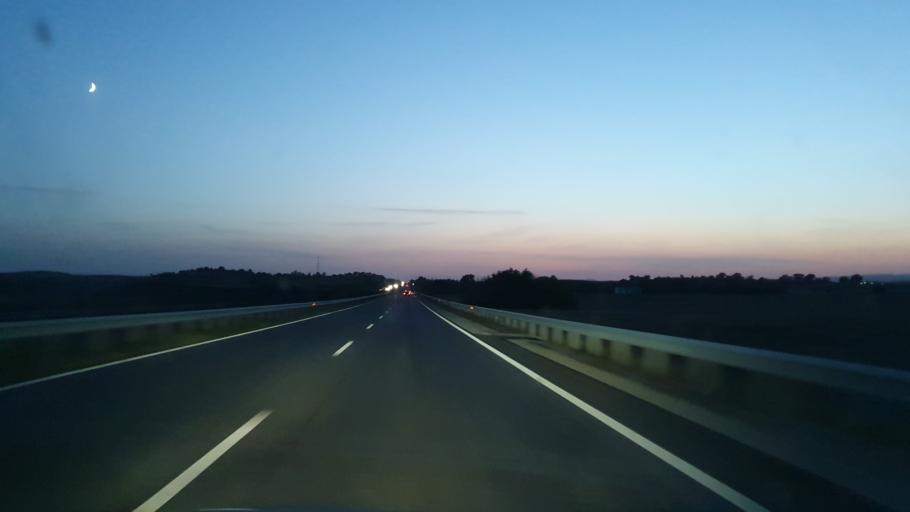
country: HU
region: Veszprem
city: Hajmasker
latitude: 47.1433
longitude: 18.0453
